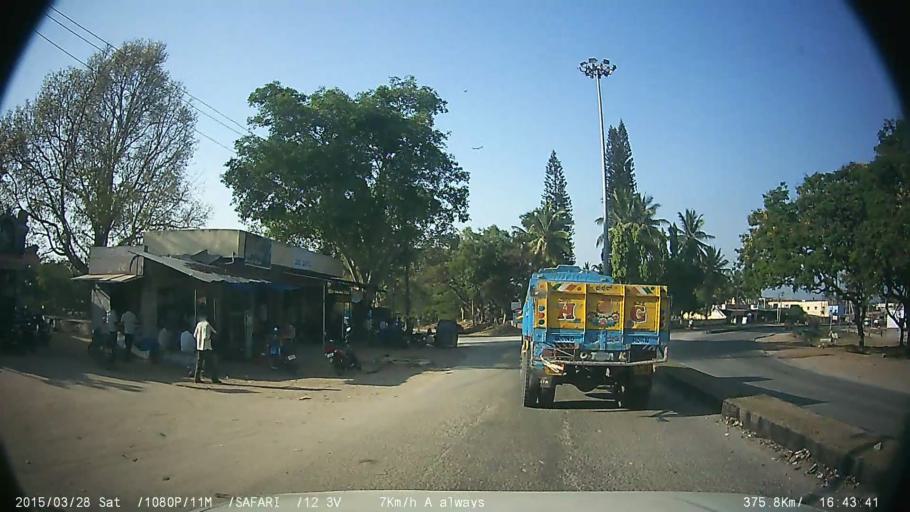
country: IN
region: Karnataka
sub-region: Mandya
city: Shrirangapattana
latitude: 12.4049
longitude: 76.5724
